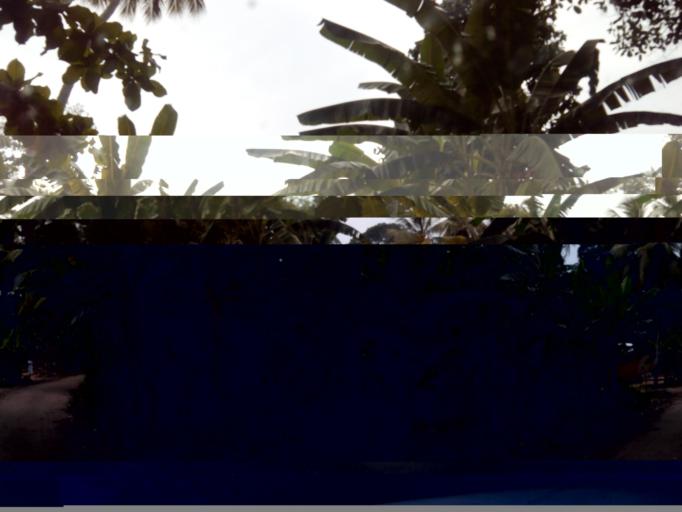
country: TZ
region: Zanzibar Central/South
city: Mahonda
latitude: -6.3310
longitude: 39.3976
